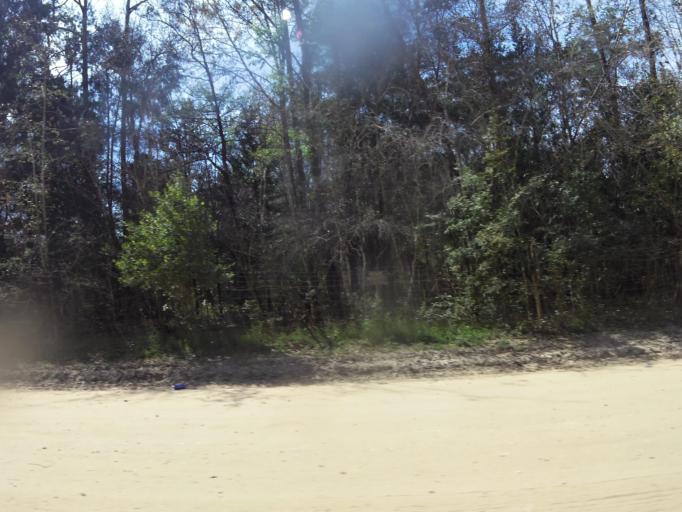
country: US
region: Florida
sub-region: Clay County
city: Middleburg
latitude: 30.1154
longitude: -81.8817
